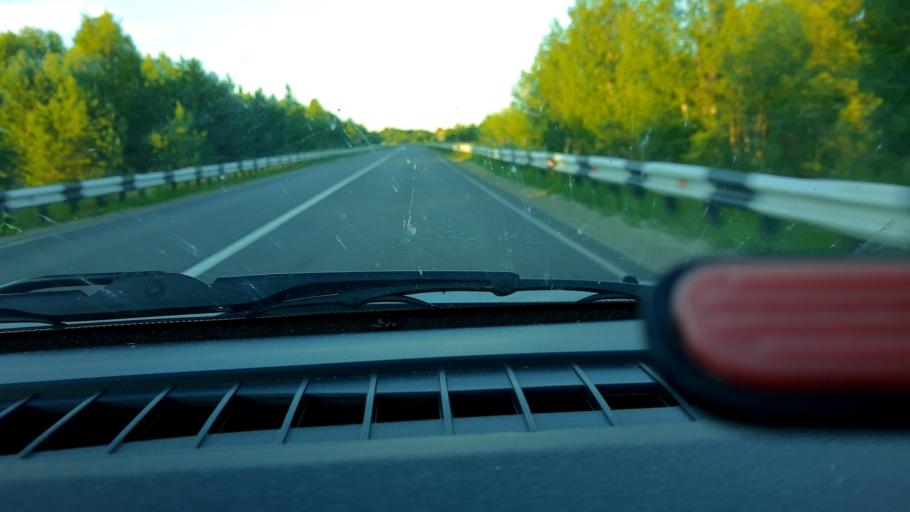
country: RU
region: Nizjnij Novgorod
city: Uren'
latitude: 57.4348
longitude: 45.7063
